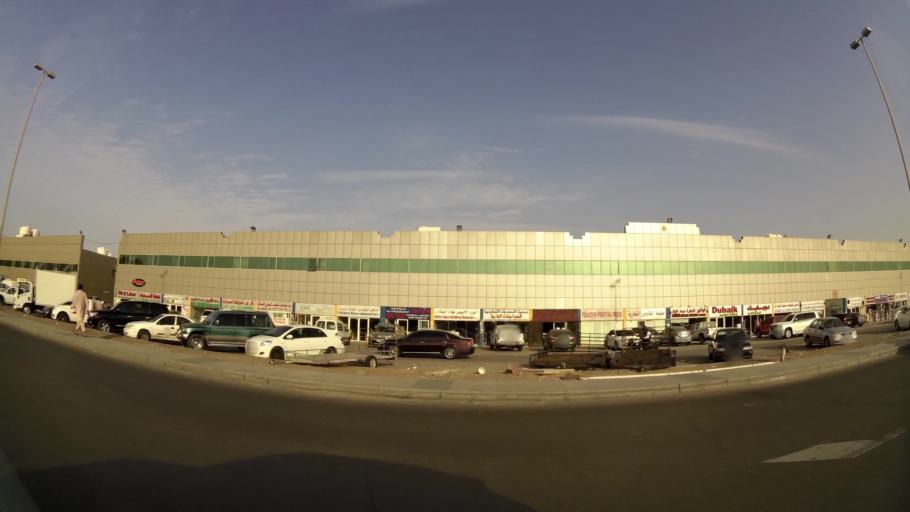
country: AE
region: Abu Dhabi
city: Abu Dhabi
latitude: 24.3720
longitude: 54.5160
